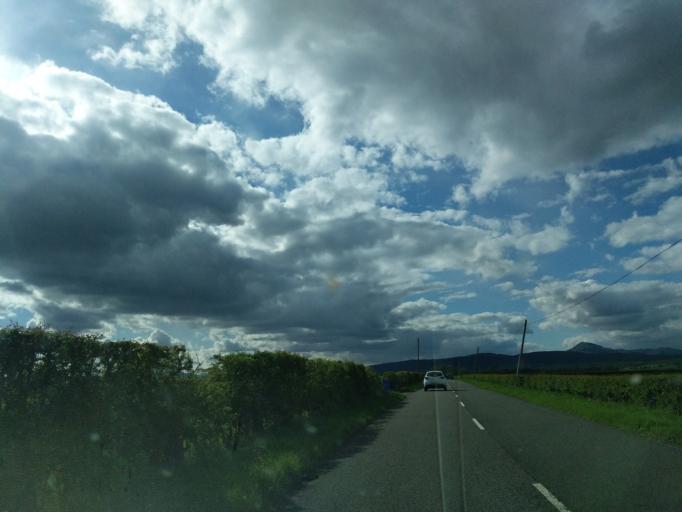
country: GB
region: Scotland
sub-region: Stirling
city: Doune
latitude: 56.1459
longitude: -4.1492
